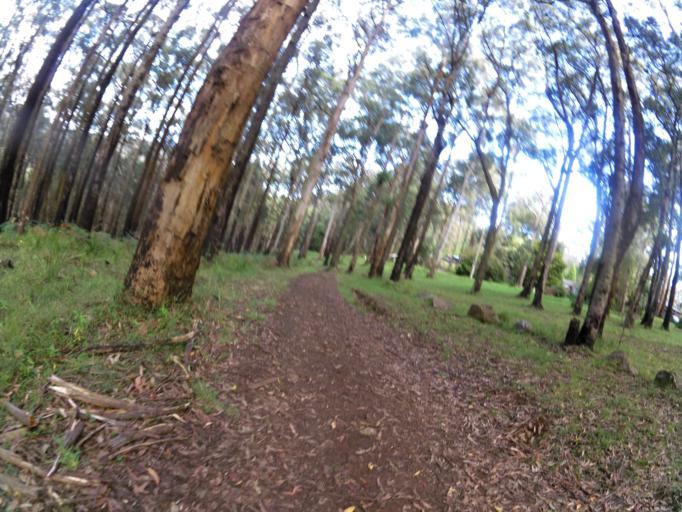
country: AU
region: Victoria
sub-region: Yarra Ranges
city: Ferny Creek
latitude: -37.8720
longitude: 145.3259
